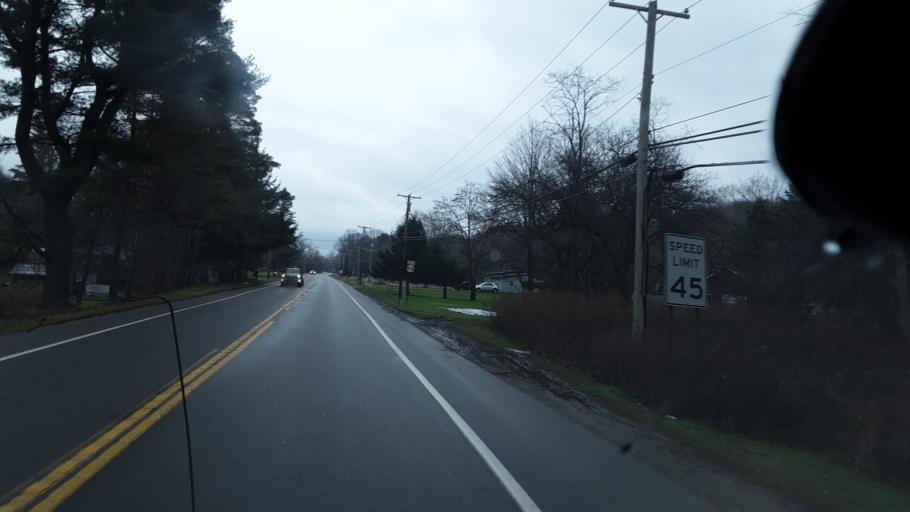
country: US
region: New York
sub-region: Wyoming County
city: Arcade
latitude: 42.4896
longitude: -78.3788
